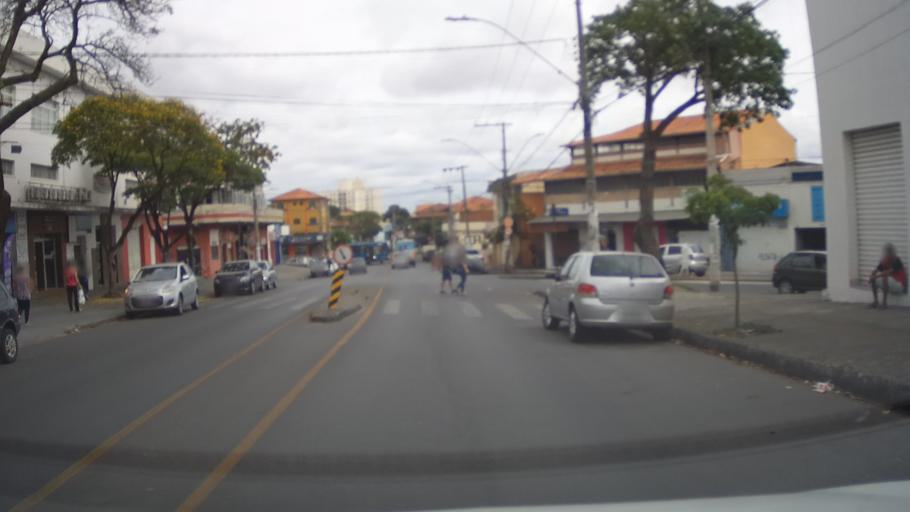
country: BR
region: Minas Gerais
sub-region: Belo Horizonte
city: Belo Horizonte
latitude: -19.8343
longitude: -43.9355
